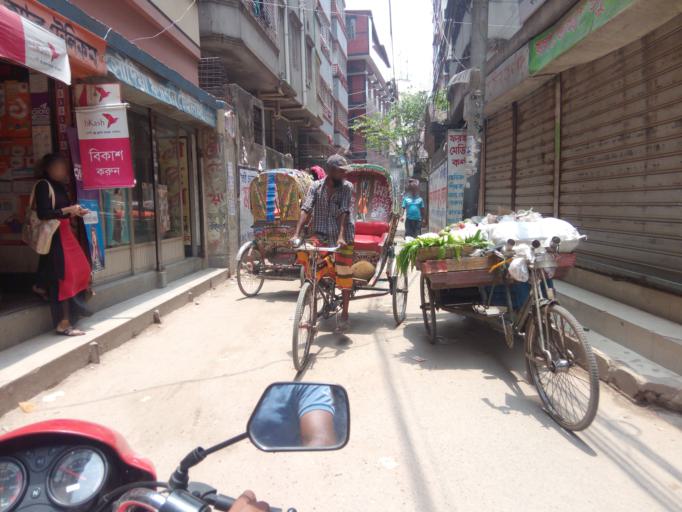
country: BD
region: Dhaka
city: Paltan
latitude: 23.7584
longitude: 90.4140
